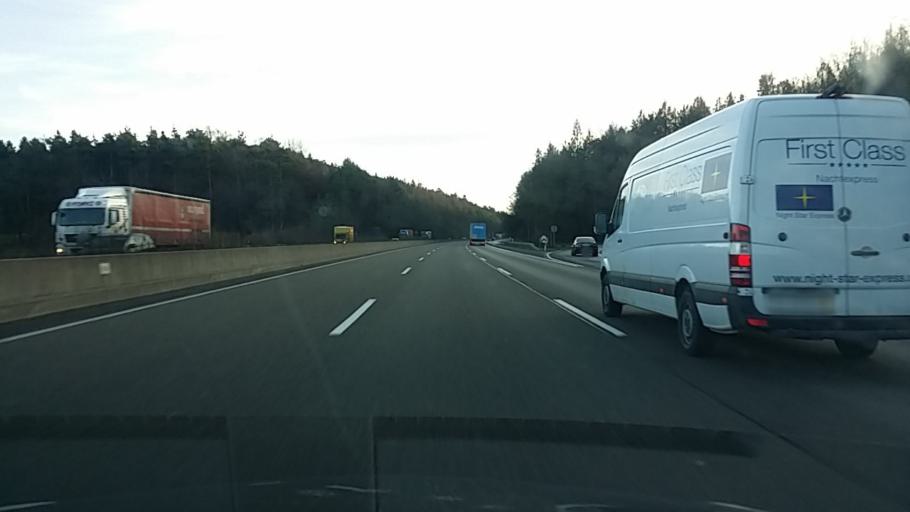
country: DE
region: Hesse
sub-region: Regierungsbezirk Kassel
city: Burghaun
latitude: 50.6517
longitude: 9.6810
